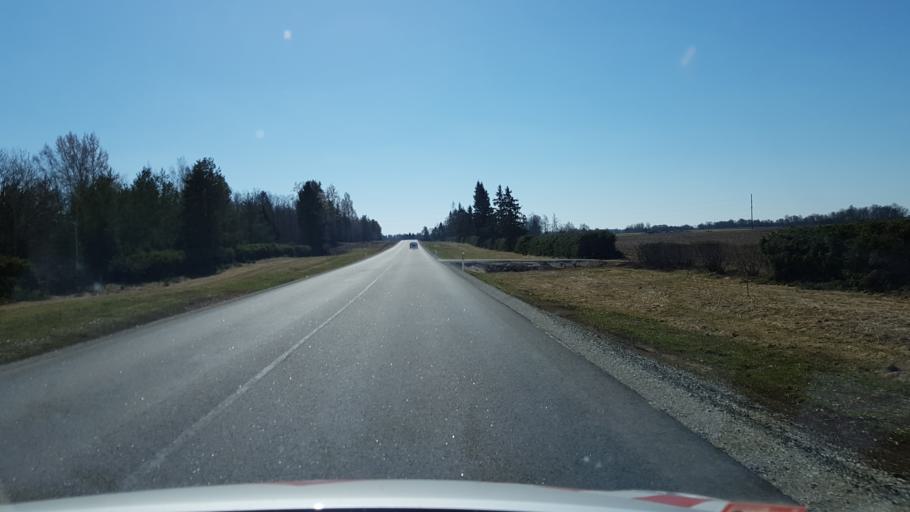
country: EE
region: Laeaene-Virumaa
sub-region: Vinni vald
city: Vinni
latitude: 59.0851
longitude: 26.6266
